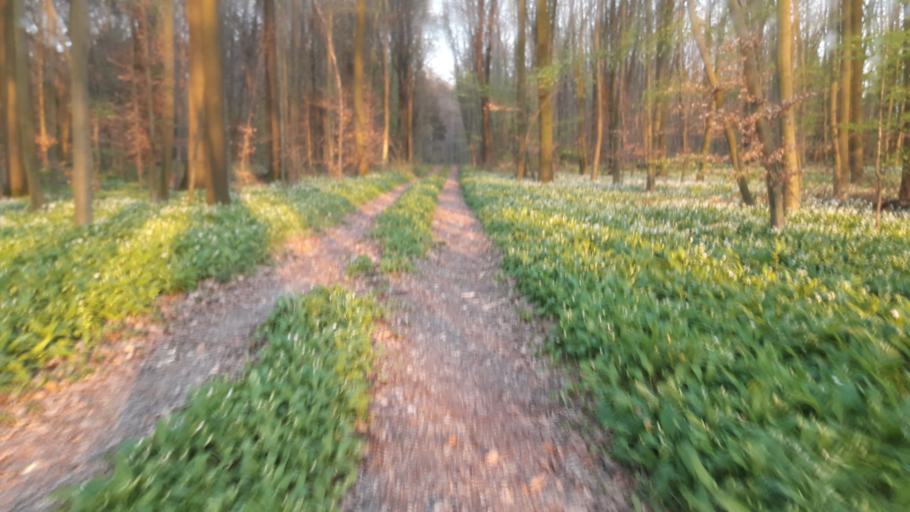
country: DE
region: North Rhine-Westphalia
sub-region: Regierungsbezirk Detmold
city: Salzkotten
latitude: 51.6667
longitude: 8.6498
